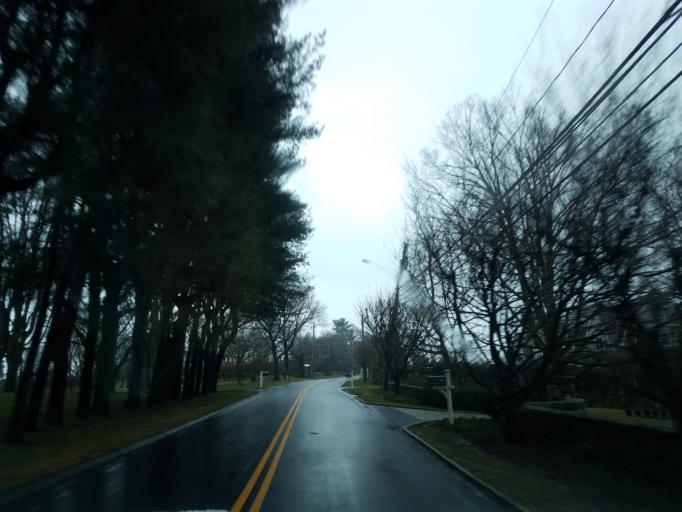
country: US
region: Connecticut
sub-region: Fairfield County
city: Southport
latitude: 41.1356
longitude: -73.3202
